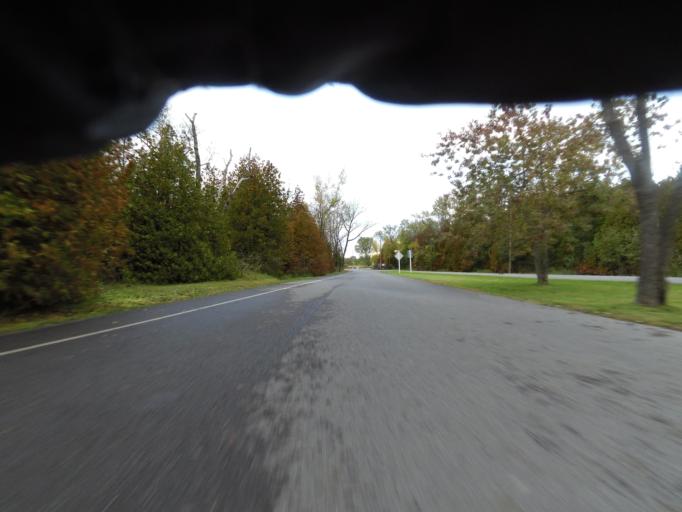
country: CA
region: Ontario
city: Quinte West
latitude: 44.0103
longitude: -77.7427
